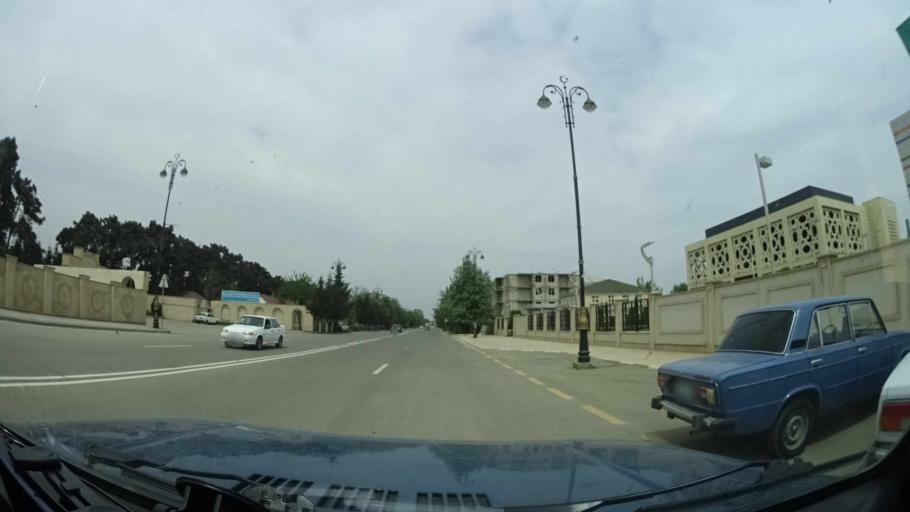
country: AZ
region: Bilasuvar Rayon
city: Pushkino
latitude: 39.4463
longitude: 48.5488
